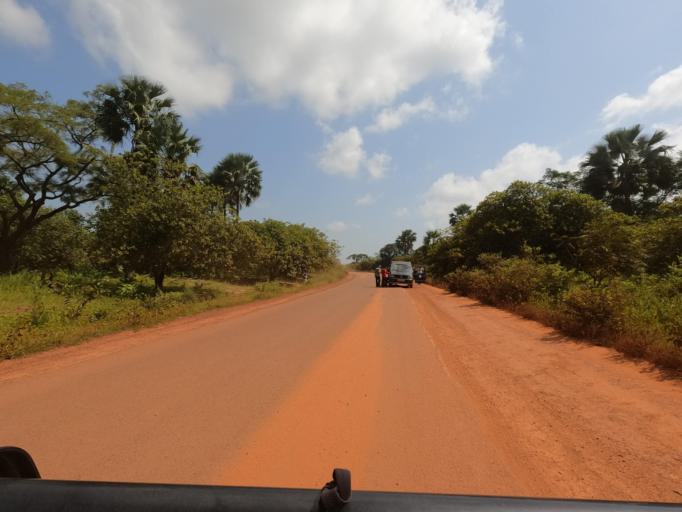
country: GW
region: Oio
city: Bissora
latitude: 12.2877
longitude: -15.7749
